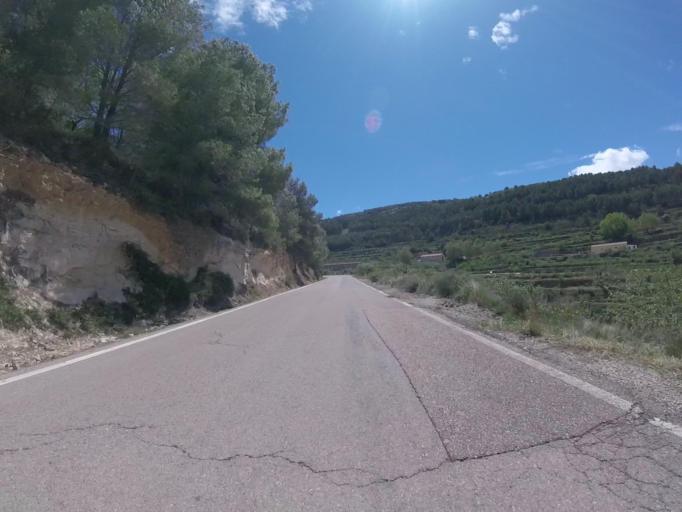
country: ES
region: Valencia
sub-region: Provincia de Castello
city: Sierra-Engarceran
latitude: 40.2724
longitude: -0.0159
